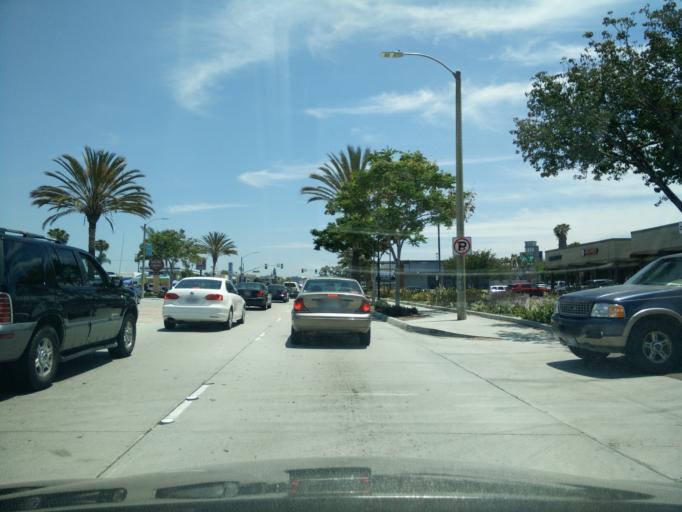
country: US
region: California
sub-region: San Diego County
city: Chula Vista
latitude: 32.6304
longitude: -117.0911
